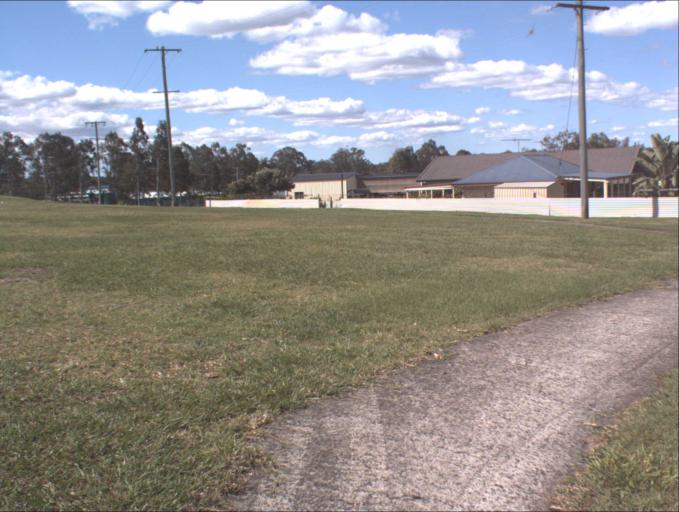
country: AU
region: Queensland
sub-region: Logan
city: Cedar Vale
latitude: -27.8312
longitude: 153.0288
